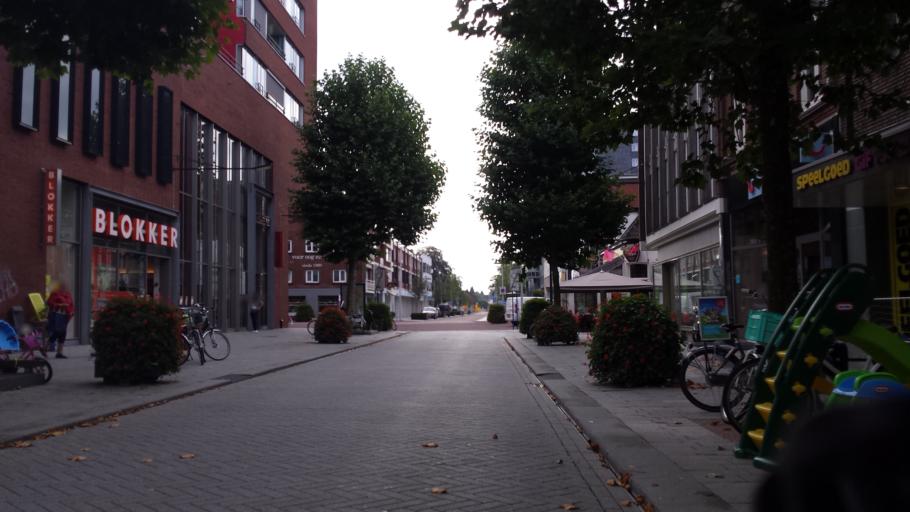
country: NL
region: Overijssel
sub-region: Gemeente Hengelo
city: Hengelo
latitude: 52.2648
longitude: 6.7946
